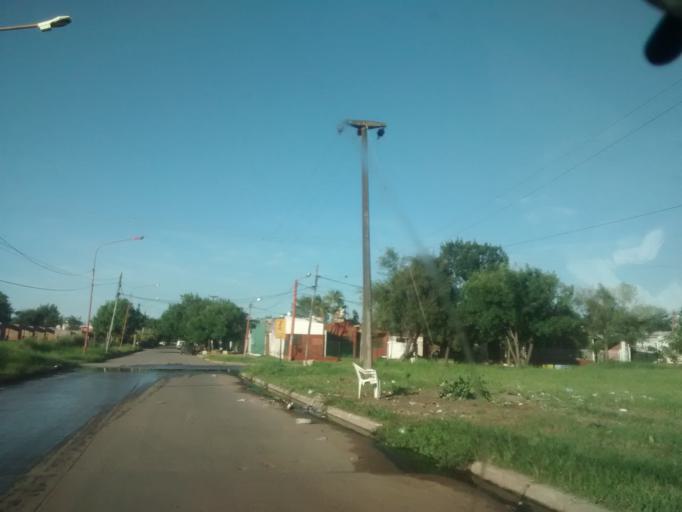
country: AR
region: Chaco
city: Resistencia
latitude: -27.4549
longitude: -59.0122
